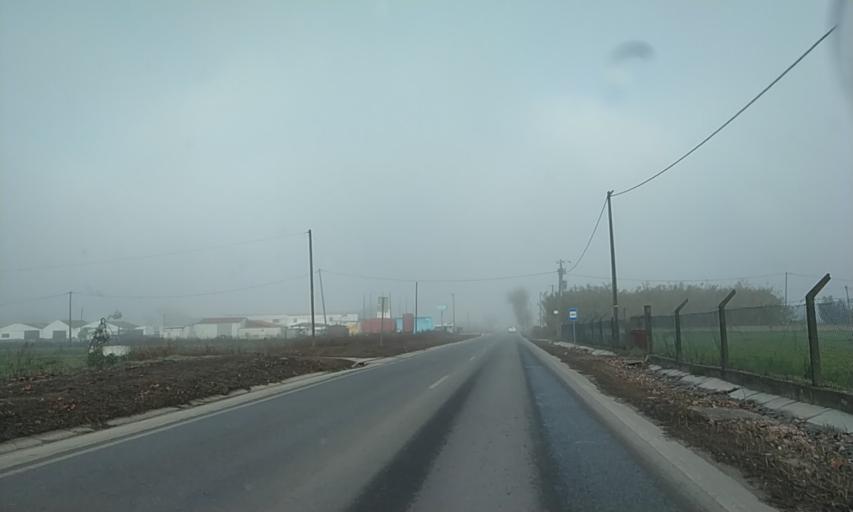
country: PT
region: Setubal
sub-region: Palmela
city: Pinhal Novo
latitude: 38.6589
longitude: -8.9215
